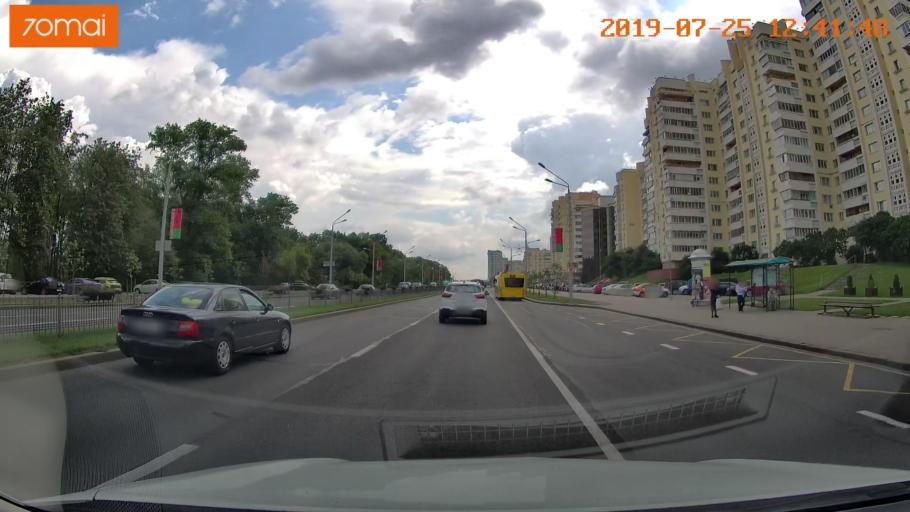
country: BY
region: Minsk
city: Minsk
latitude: 53.9199
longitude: 27.5304
